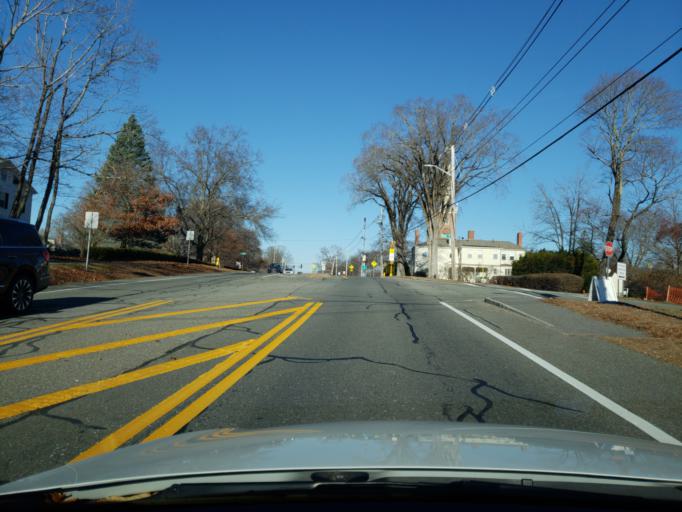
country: US
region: Massachusetts
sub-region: Essex County
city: Andover
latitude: 42.6442
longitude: -71.1322
